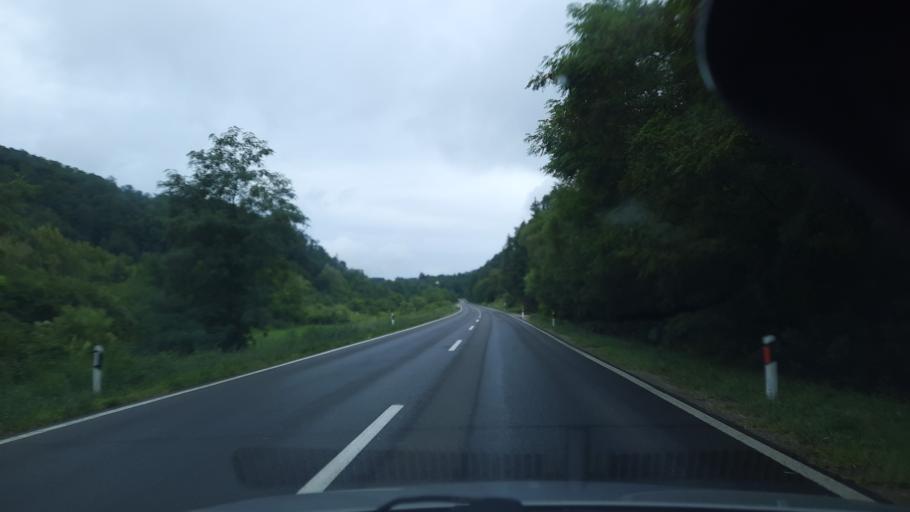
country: RS
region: Central Serbia
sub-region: Sumadijski Okrug
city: Knic
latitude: 43.9603
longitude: 20.8084
